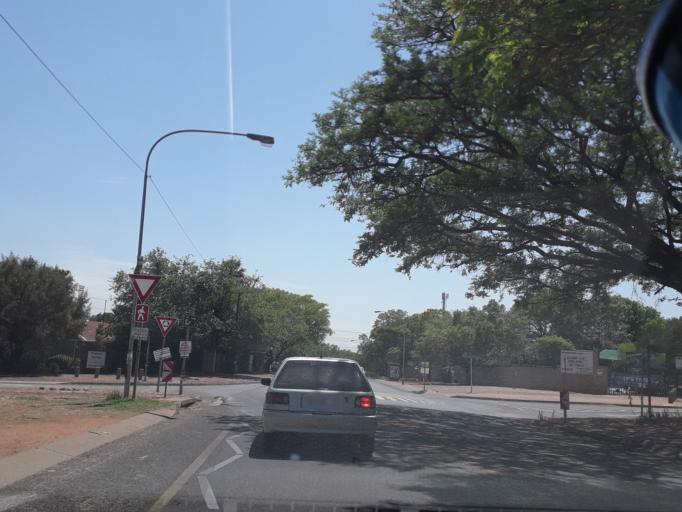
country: ZA
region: Gauteng
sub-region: City of Tshwane Metropolitan Municipality
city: Centurion
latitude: -25.8894
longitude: 28.1507
